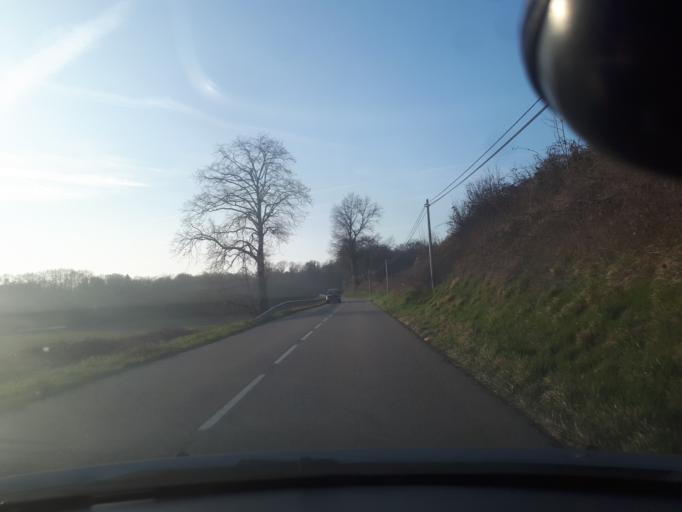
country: FR
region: Rhone-Alpes
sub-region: Departement de l'Isere
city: Sermerieu
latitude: 45.6681
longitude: 5.4396
